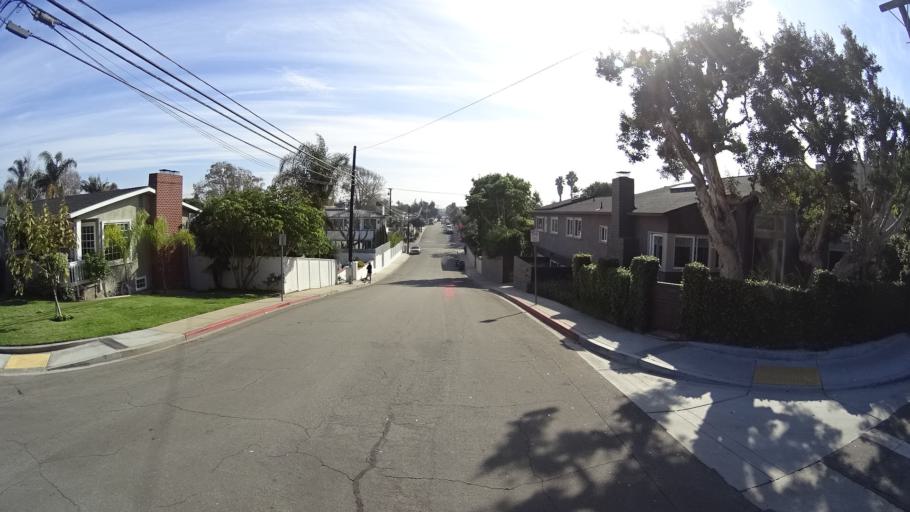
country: US
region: California
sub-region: Los Angeles County
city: Hermosa Beach
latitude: 33.8757
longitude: -118.3852
